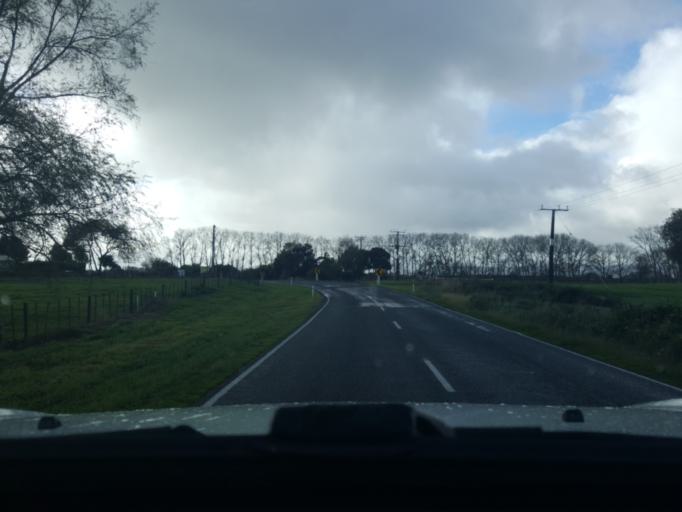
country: NZ
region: Waikato
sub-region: Waikato District
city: Te Kauwhata
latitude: -37.4429
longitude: 175.1248
